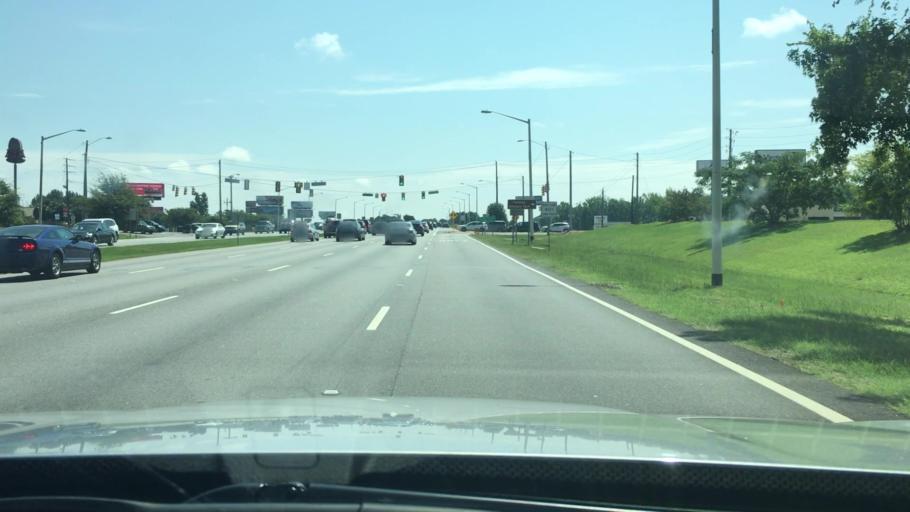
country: US
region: South Carolina
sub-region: Florence County
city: Florence
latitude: 34.1882
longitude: -79.8261
